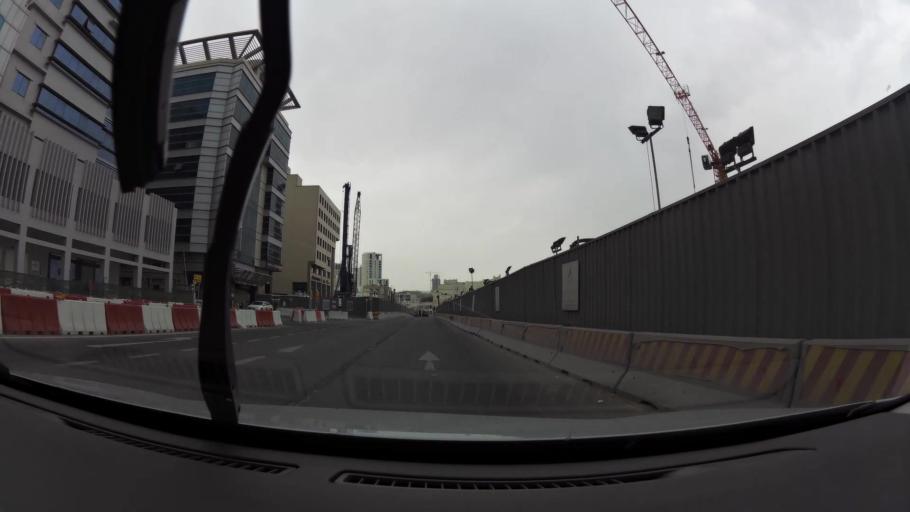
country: QA
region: Baladiyat ad Dawhah
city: Doha
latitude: 25.2863
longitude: 51.5366
